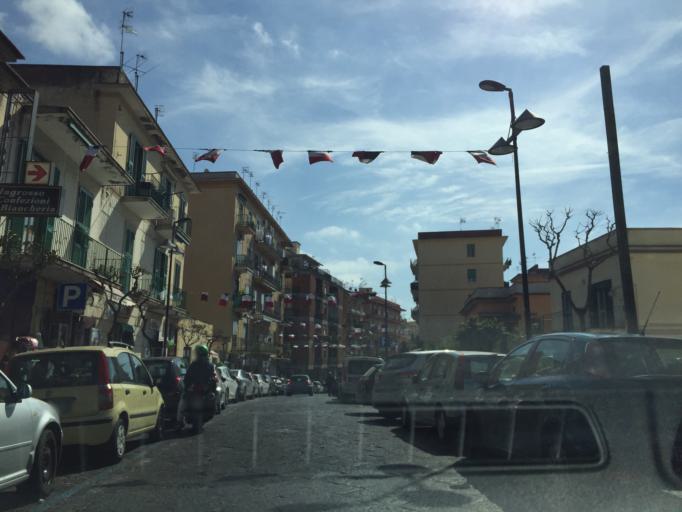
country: IT
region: Campania
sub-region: Provincia di Napoli
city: Ercolano
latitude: 40.8106
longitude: 14.3527
